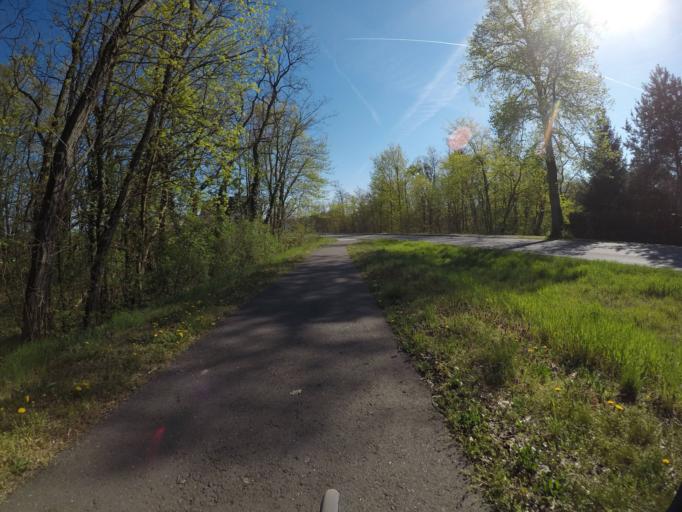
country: DE
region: Brandenburg
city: Rehfelde
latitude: 52.4669
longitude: 13.9063
